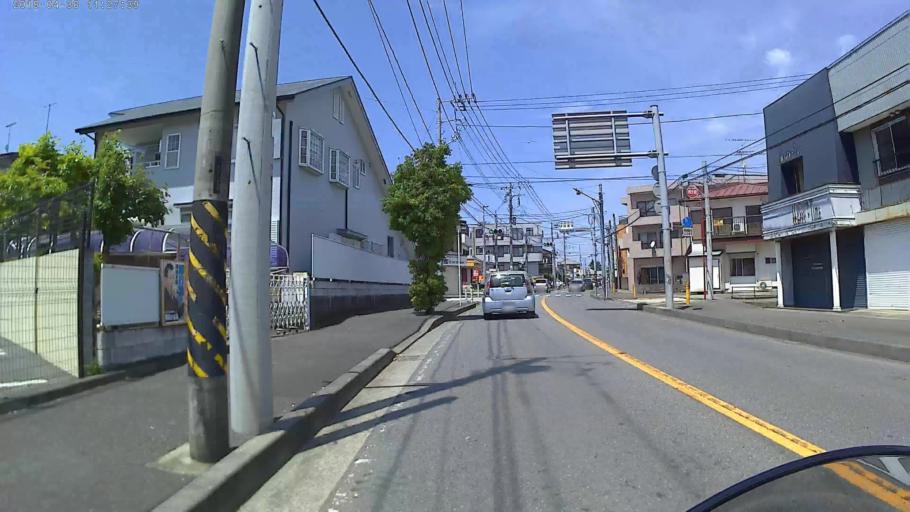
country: JP
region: Kanagawa
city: Zama
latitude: 35.4796
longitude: 139.4124
